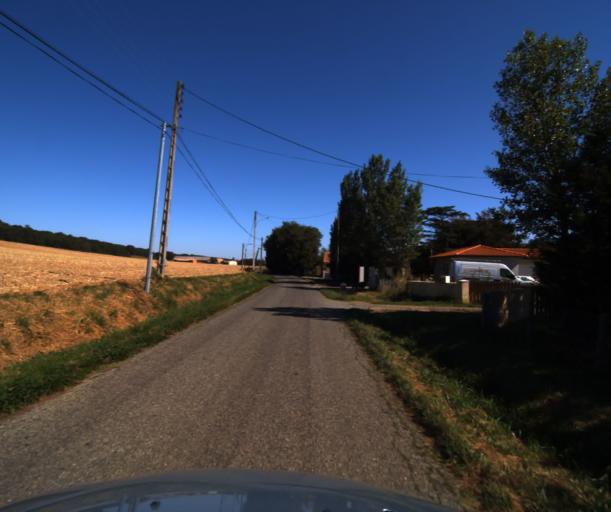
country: FR
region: Midi-Pyrenees
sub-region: Departement de la Haute-Garonne
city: Eaunes
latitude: 43.4132
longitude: 1.3545
